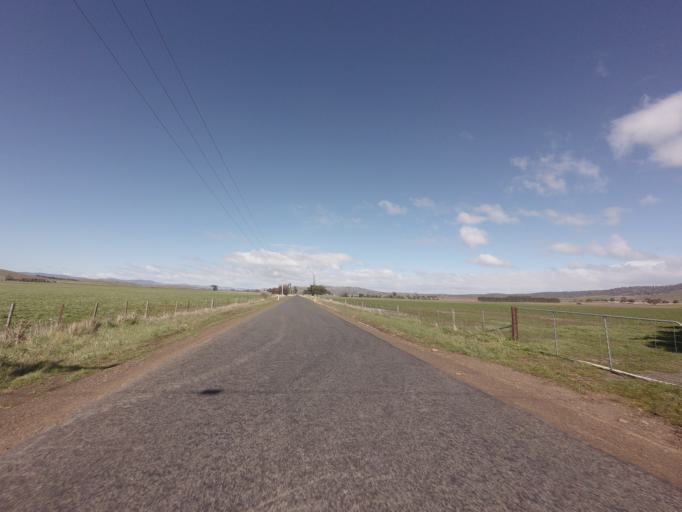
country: AU
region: Tasmania
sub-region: Northern Midlands
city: Evandale
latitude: -41.9940
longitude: 147.4536
